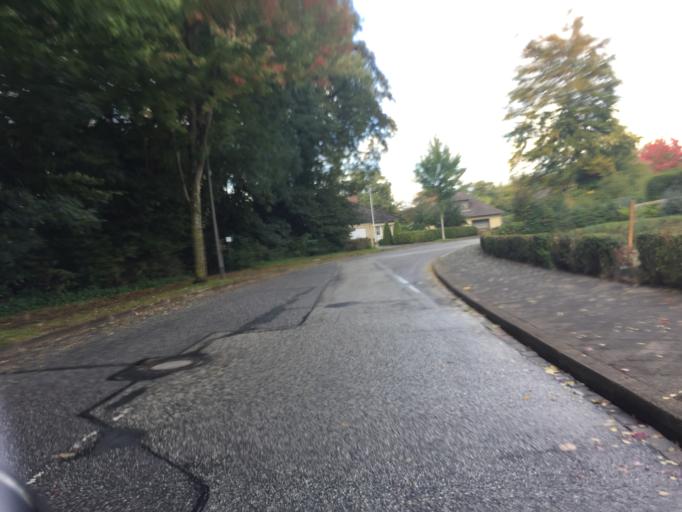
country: DE
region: Schleswig-Holstein
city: Heiligenstedten
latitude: 53.9394
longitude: 9.4914
